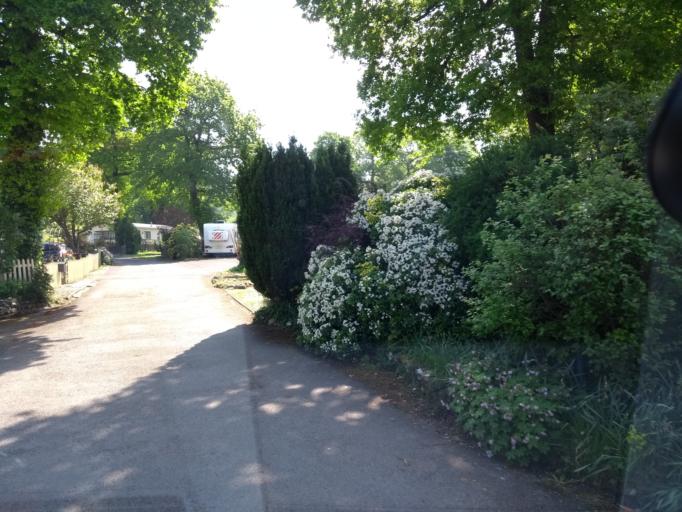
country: GB
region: England
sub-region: Somerset
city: Chard
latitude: 50.8803
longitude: -3.0282
